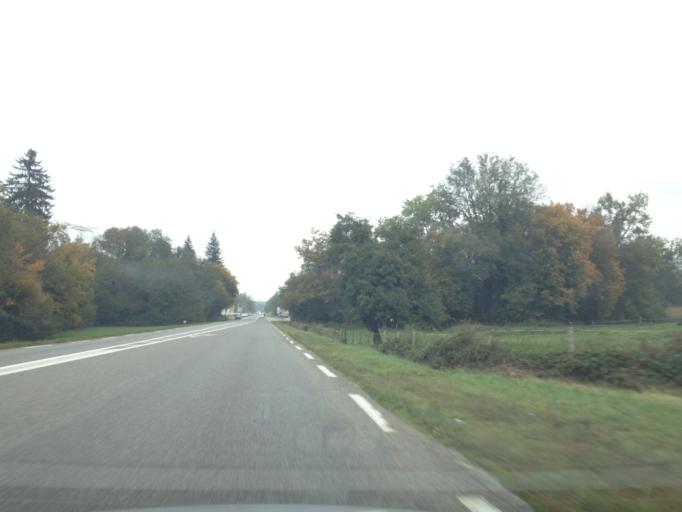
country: FR
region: Rhone-Alpes
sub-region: Departement de la Haute-Savoie
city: Viuz-la-Chiesaz
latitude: 45.8501
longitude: 6.0609
